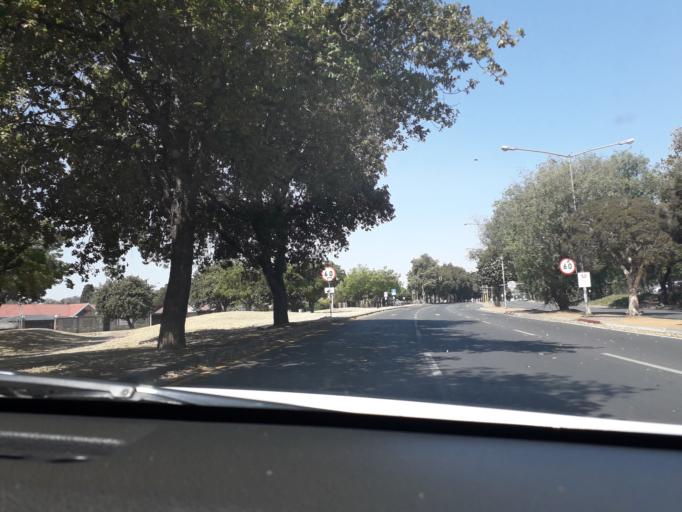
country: ZA
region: Gauteng
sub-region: City of Johannesburg Metropolitan Municipality
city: Modderfontein
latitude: -26.1008
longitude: 28.2262
